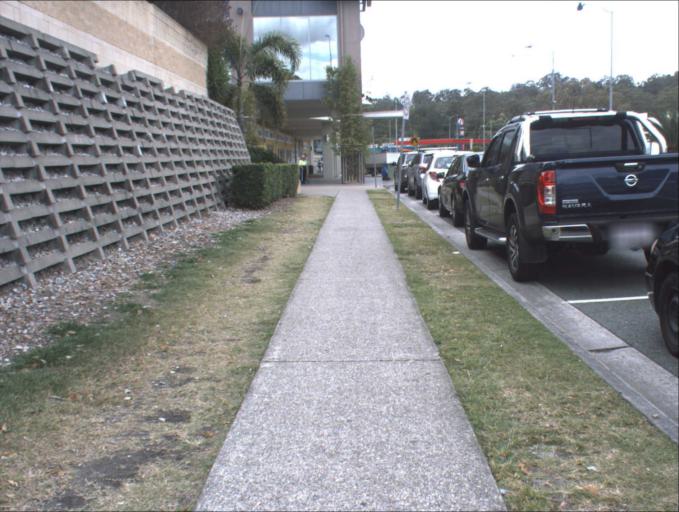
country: AU
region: Queensland
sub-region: Logan
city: Slacks Creek
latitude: -27.6579
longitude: 153.1697
